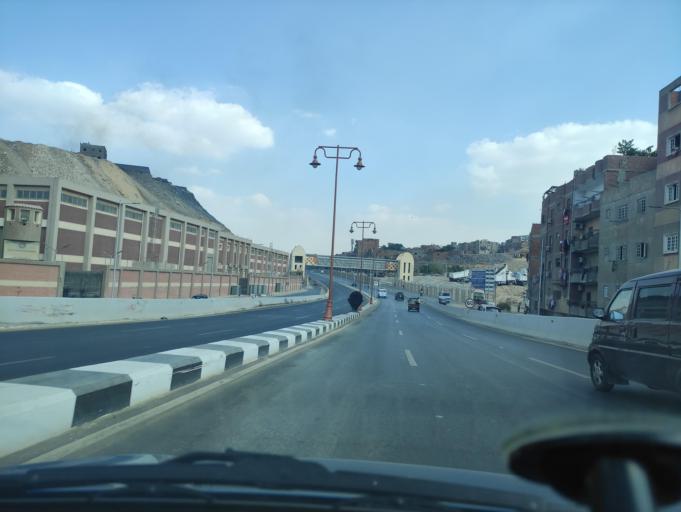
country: EG
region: Muhafazat al Qahirah
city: Cairo
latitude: 30.0471
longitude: 31.2877
